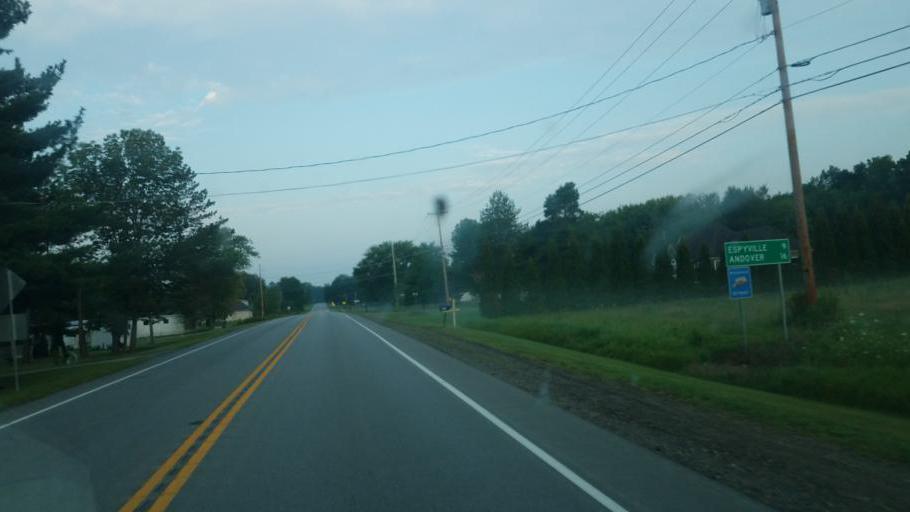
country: US
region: Pennsylvania
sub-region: Crawford County
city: Conneaut Lakeshore
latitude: 41.6035
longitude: -80.3182
